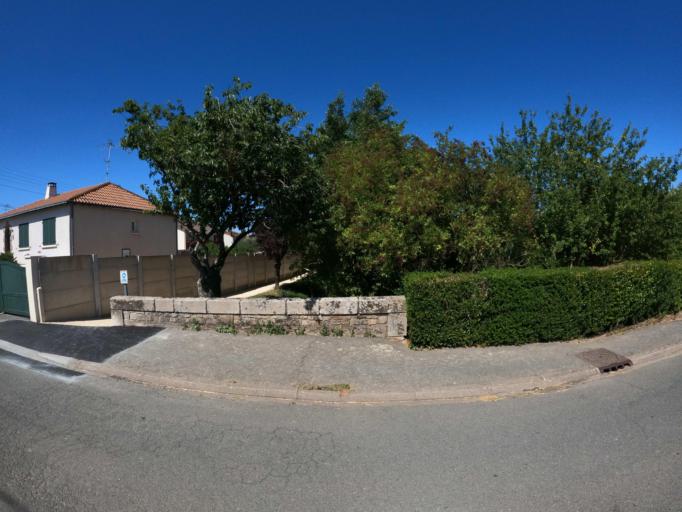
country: FR
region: Pays de la Loire
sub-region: Departement de Maine-et-Loire
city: Saint-Christophe-du-Bois
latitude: 47.0273
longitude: -0.9481
